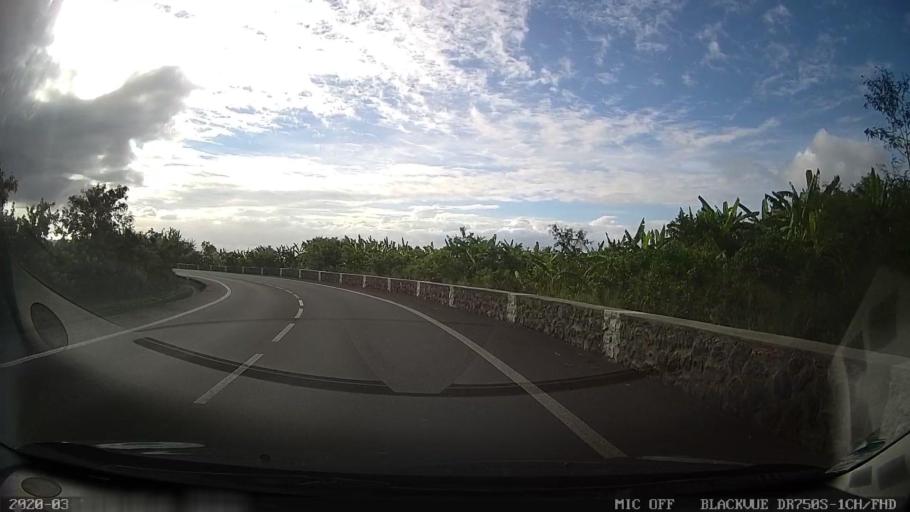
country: RE
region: Reunion
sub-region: Reunion
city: Saint-Paul
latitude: -21.0646
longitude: 55.2436
